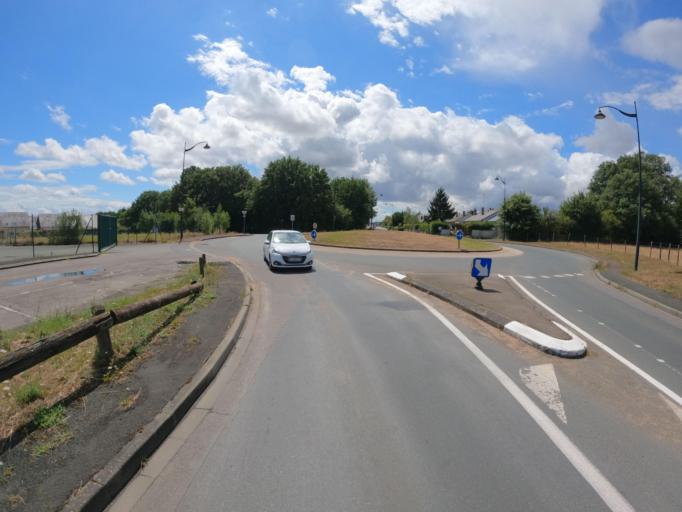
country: FR
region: Pays de la Loire
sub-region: Departement de Maine-et-Loire
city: Feneu
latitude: 47.5762
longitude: -0.5927
